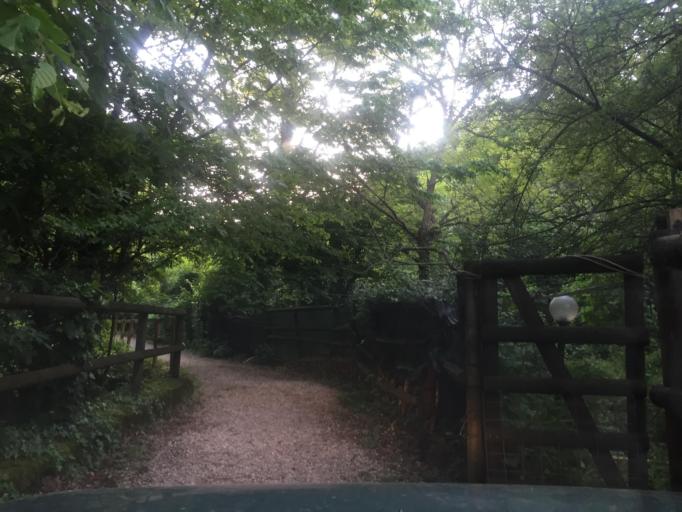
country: IT
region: Friuli Venezia Giulia
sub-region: Provincia di Trieste
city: Trieste
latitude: 45.6487
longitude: 13.8135
